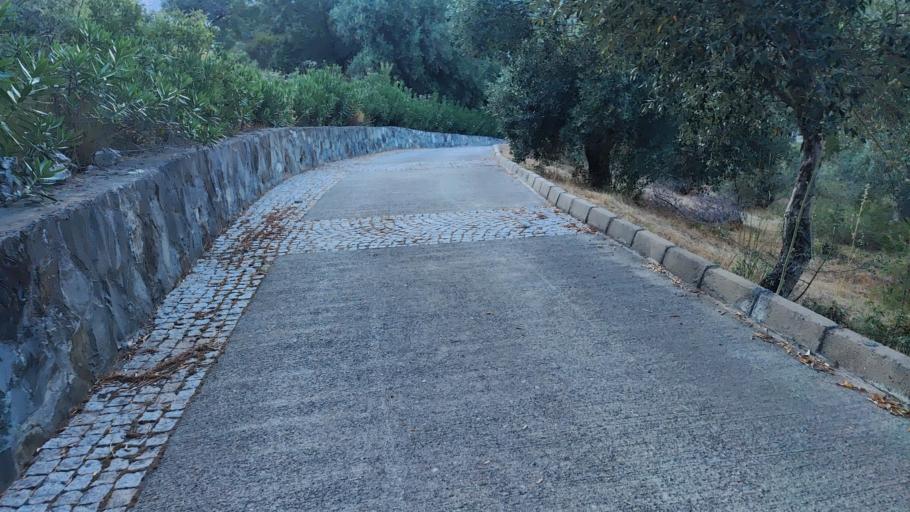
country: TR
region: Mugla
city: Sarigerme
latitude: 36.7057
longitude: 28.6931
